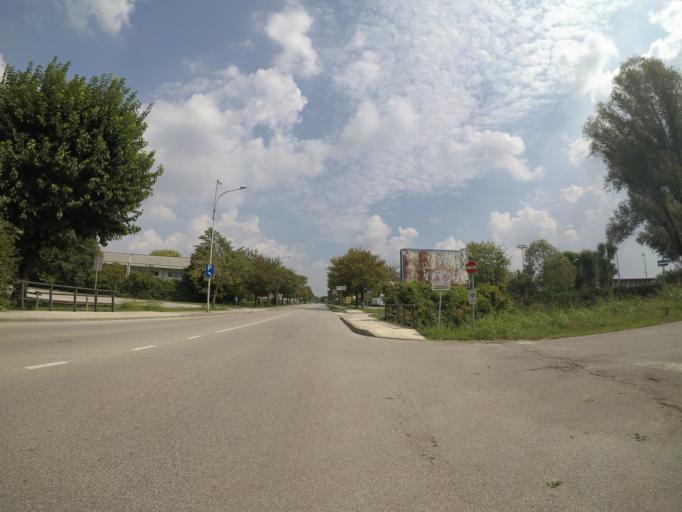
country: IT
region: Friuli Venezia Giulia
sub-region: Provincia di Udine
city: Codroipo
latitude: 45.9560
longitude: 12.9803
